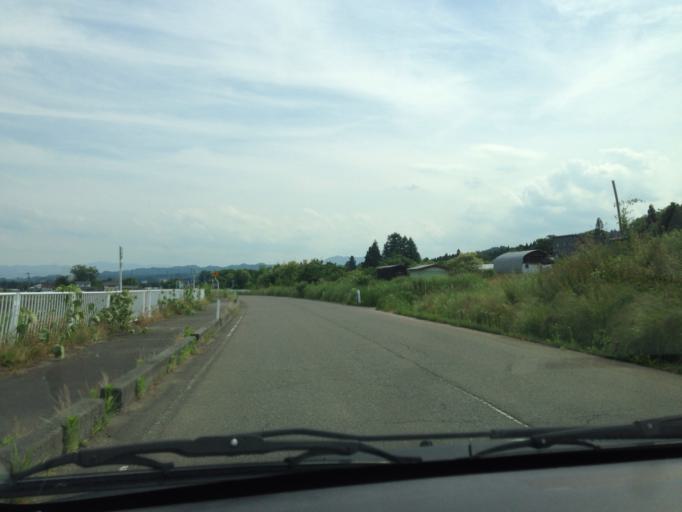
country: JP
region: Fukushima
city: Kitakata
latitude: 37.5516
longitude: 139.7991
